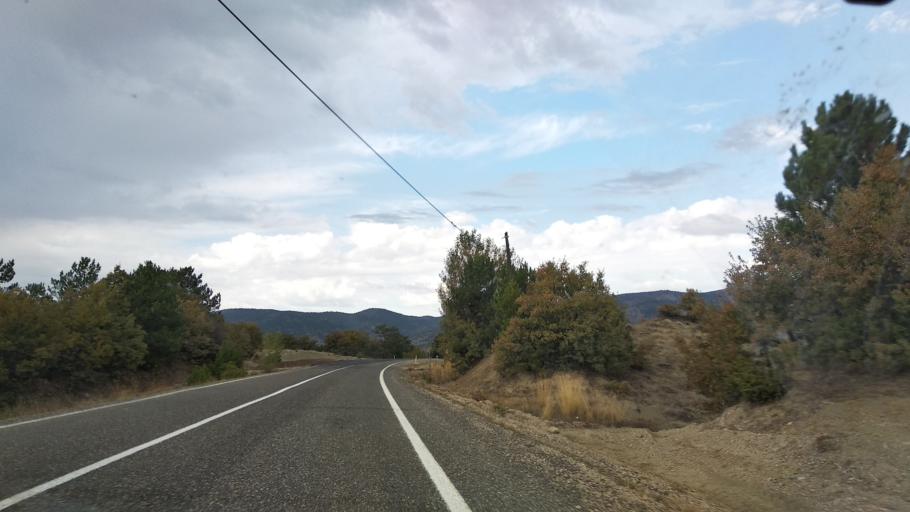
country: TR
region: Bolu
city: Seben
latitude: 40.3336
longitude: 31.4412
